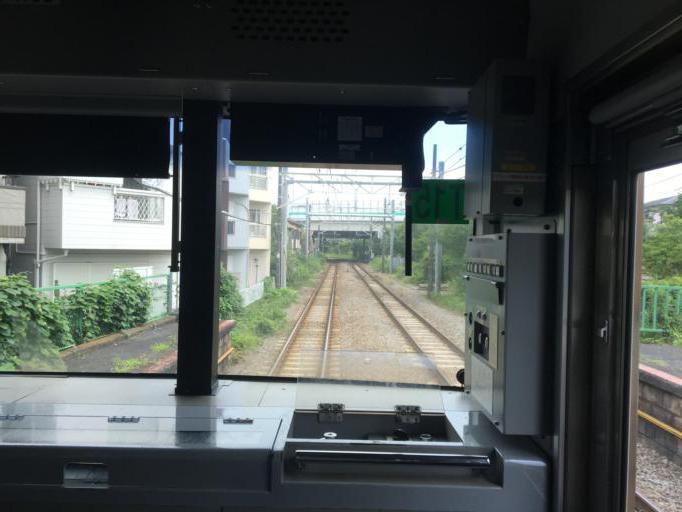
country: JP
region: Kanagawa
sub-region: Kawasaki-shi
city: Kawasaki
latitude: 35.4968
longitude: 139.6815
